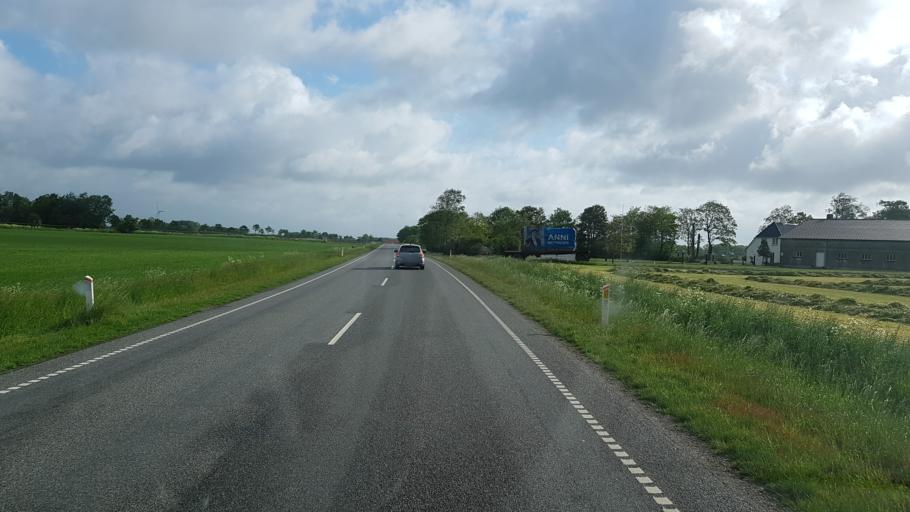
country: DK
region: South Denmark
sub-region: Vejen Kommune
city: Vejen
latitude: 55.4132
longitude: 9.1341
